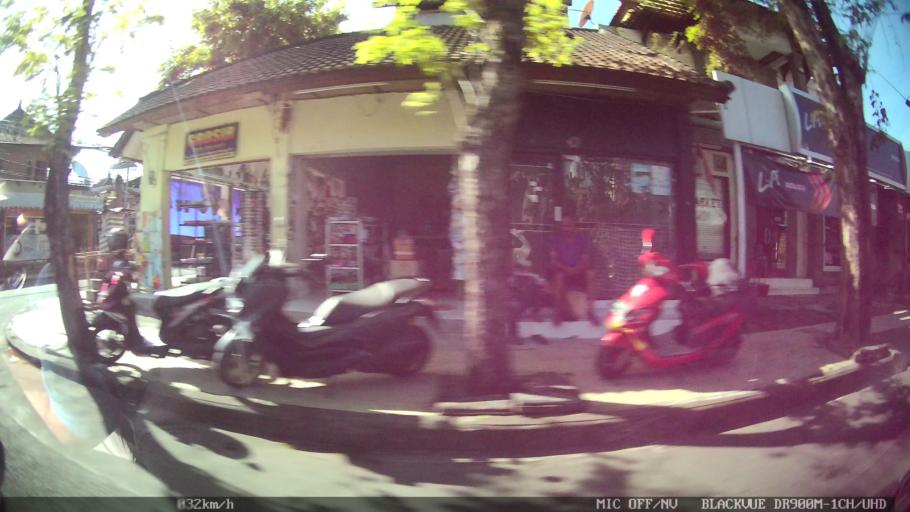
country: ID
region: Bali
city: Jabajero
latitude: -8.7247
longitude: 115.1755
